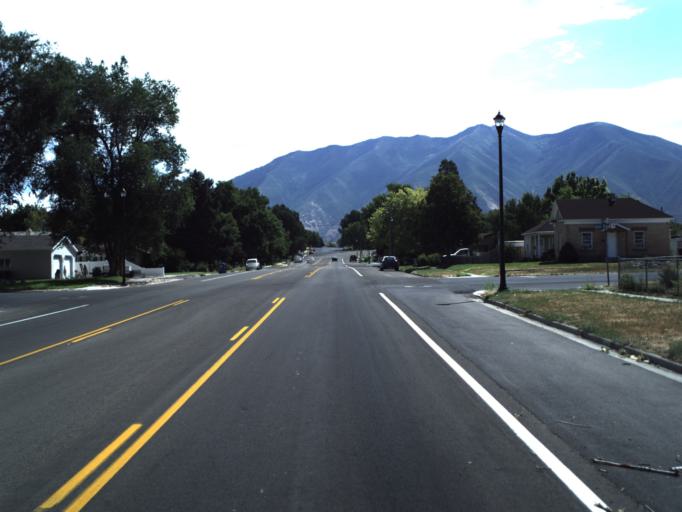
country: US
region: Utah
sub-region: Utah County
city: Spanish Fork
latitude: 40.1058
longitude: -111.6484
